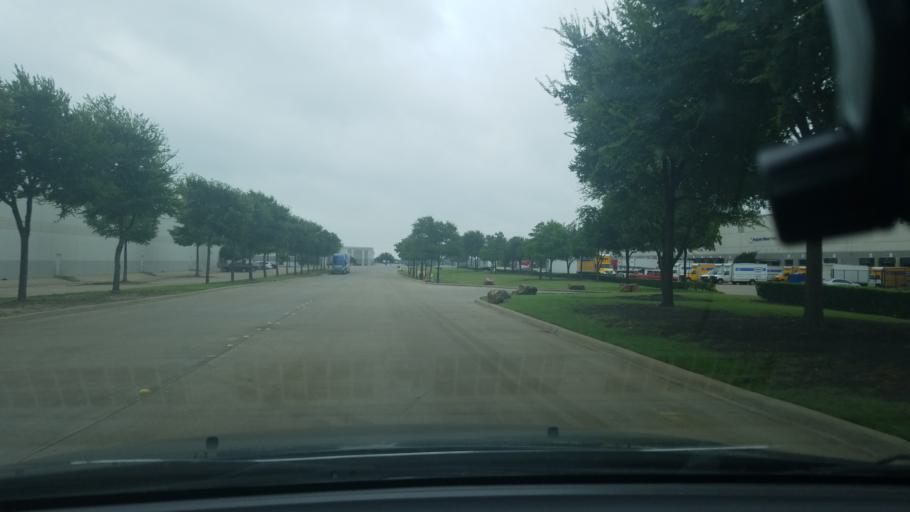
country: US
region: Texas
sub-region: Dallas County
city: Mesquite
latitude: 32.7810
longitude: -96.6521
